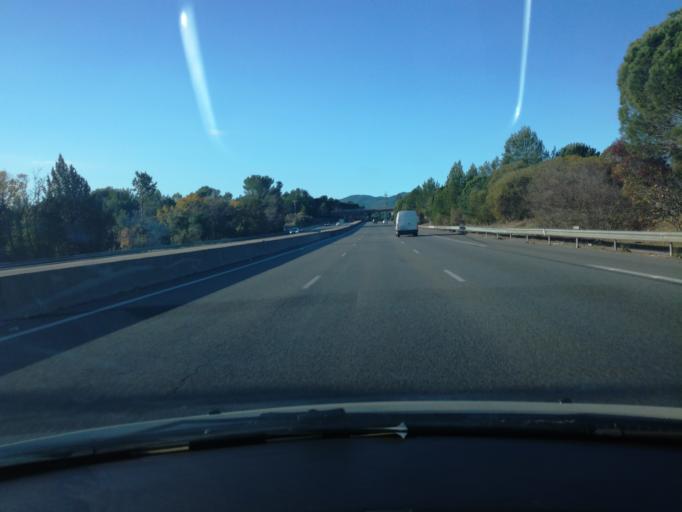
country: FR
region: Provence-Alpes-Cote d'Azur
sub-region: Departement du Var
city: Puget-sur-Argens
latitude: 43.4610
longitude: 6.7116
